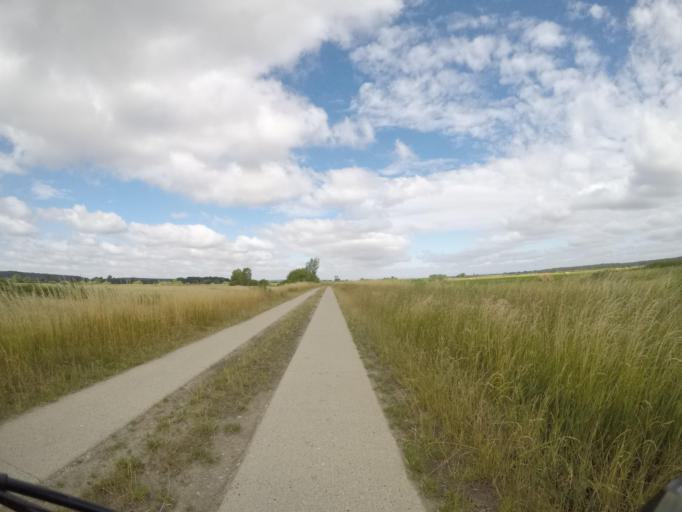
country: DE
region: Lower Saxony
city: Hitzacker
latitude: 53.1706
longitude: 11.0581
